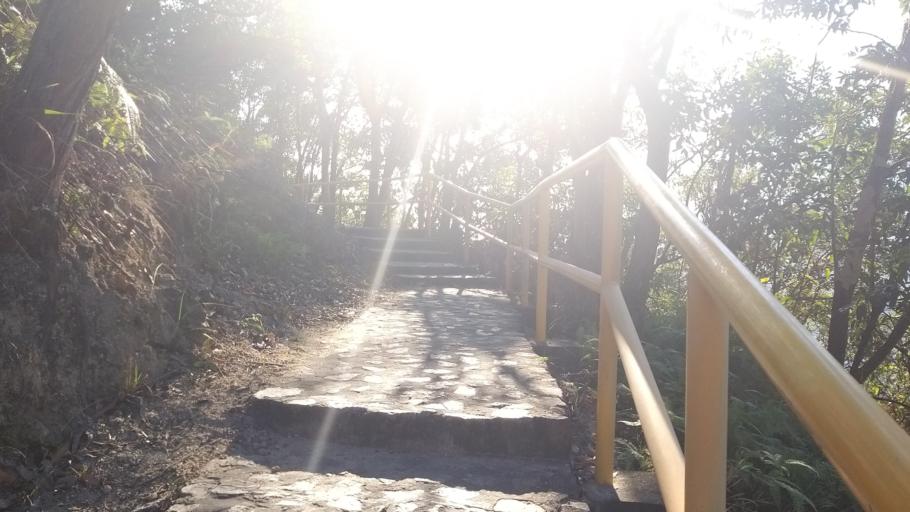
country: HK
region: Tuen Mun
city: Tuen Mun
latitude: 22.3978
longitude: 113.9836
